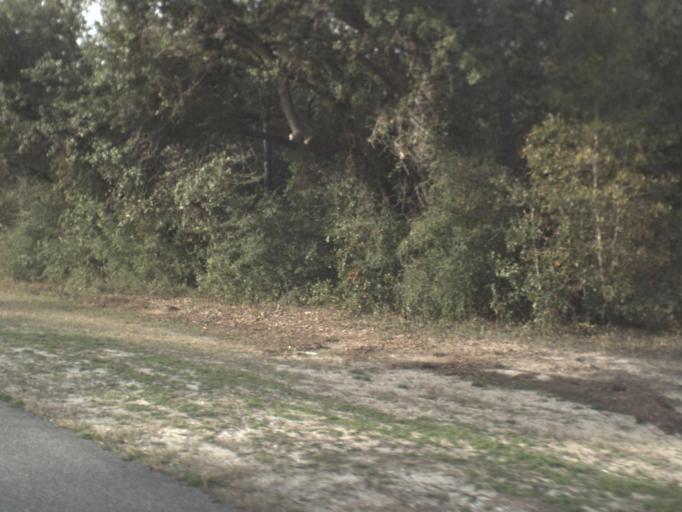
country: US
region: Florida
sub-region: Bay County
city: Mexico Beach
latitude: 29.9588
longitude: -85.4363
